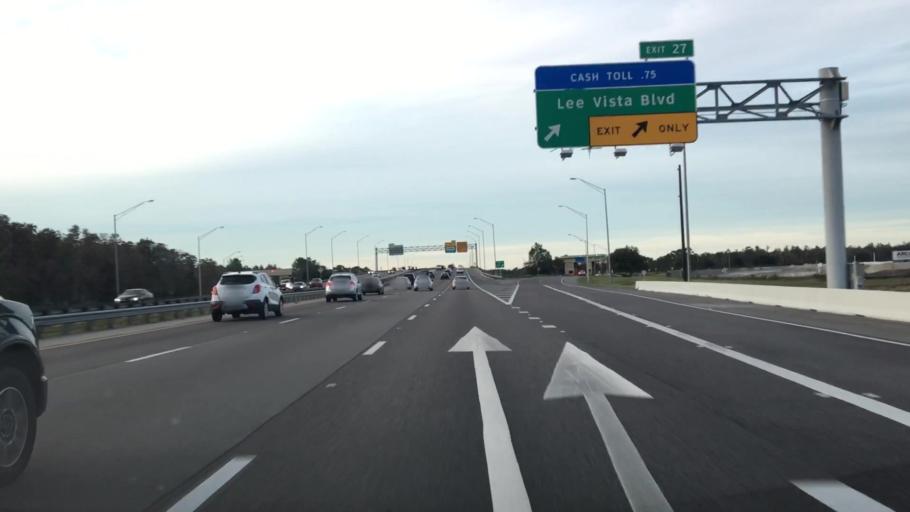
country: US
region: Florida
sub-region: Orange County
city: Azalea Park
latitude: 28.4730
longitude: -81.2382
